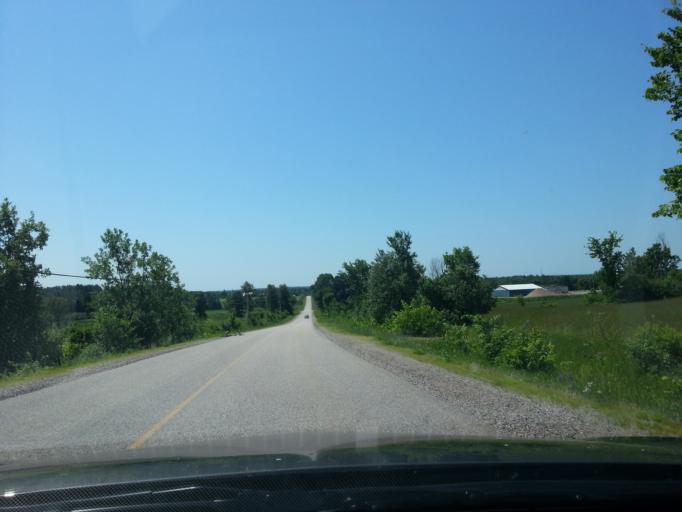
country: CA
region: Ontario
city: Arnprior
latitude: 45.5349
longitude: -76.3700
